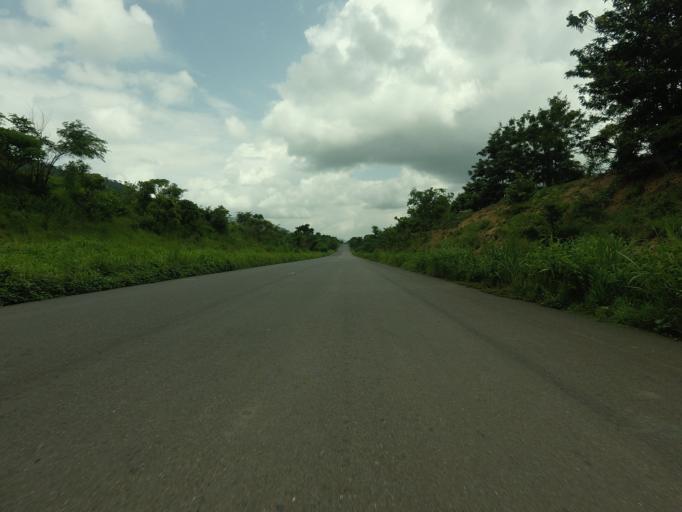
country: GH
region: Volta
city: Ho
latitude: 6.6137
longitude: 0.3021
